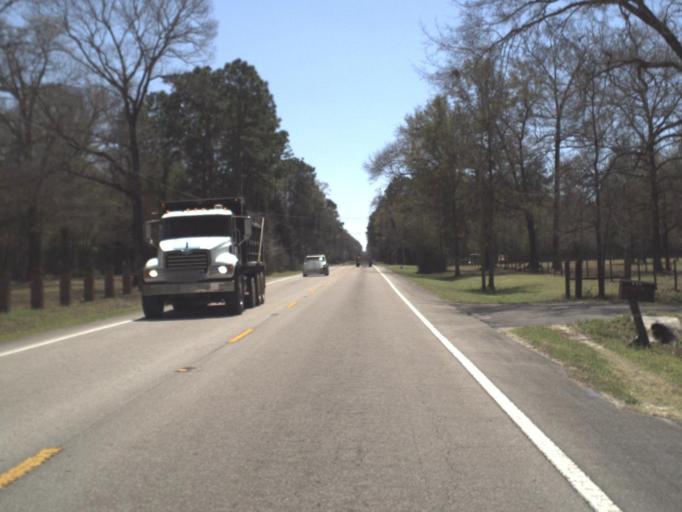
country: US
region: Florida
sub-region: Leon County
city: Woodville
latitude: 30.2634
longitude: -84.2367
